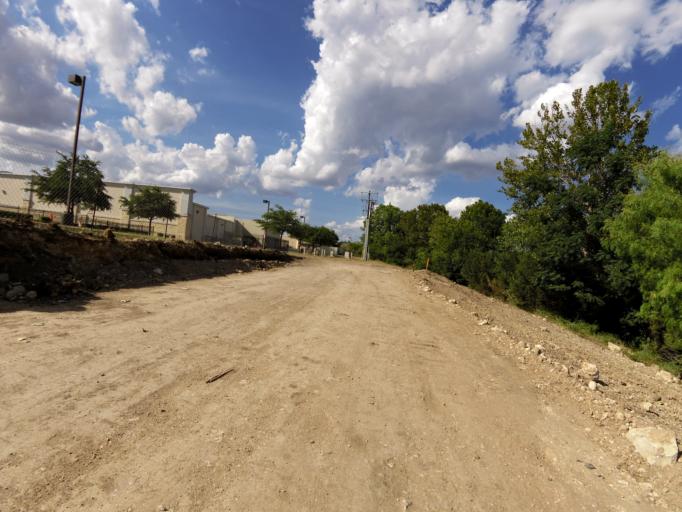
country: US
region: Texas
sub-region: Bexar County
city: Shavano Park
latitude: 29.6064
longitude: -98.5950
